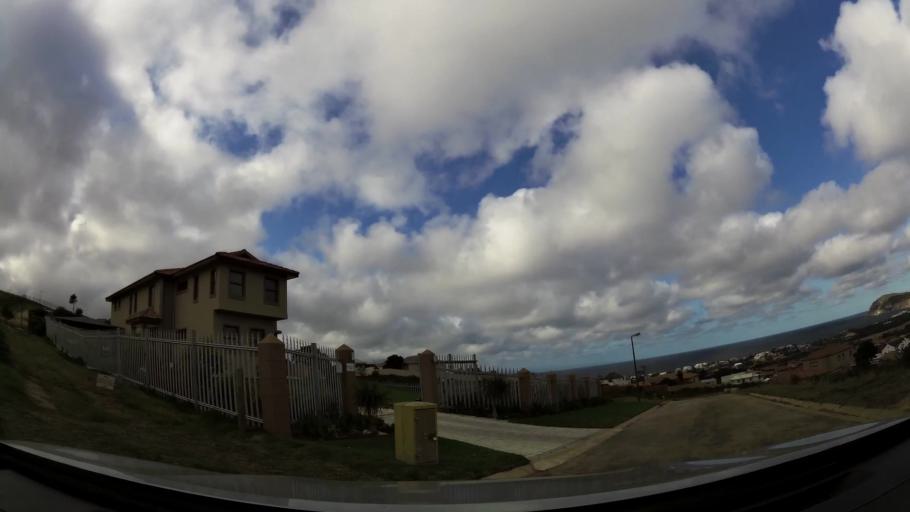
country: ZA
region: Western Cape
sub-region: Eden District Municipality
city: Plettenberg Bay
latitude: -34.0849
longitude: 23.3564
